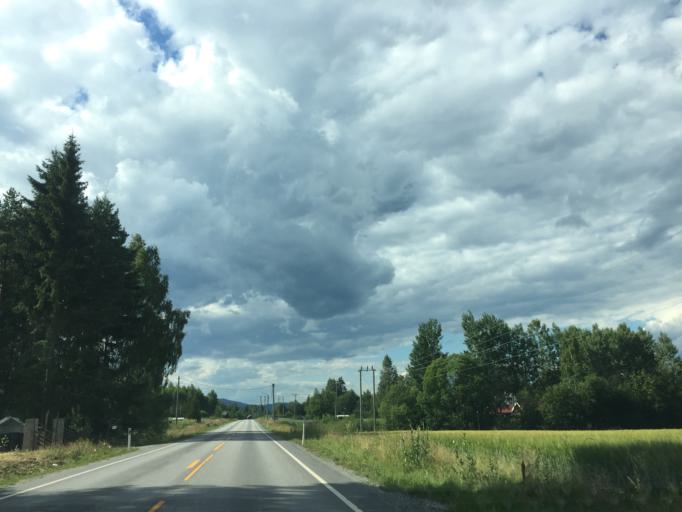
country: NO
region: Hedmark
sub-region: Sor-Odal
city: Skarnes
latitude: 60.2447
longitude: 11.7086
